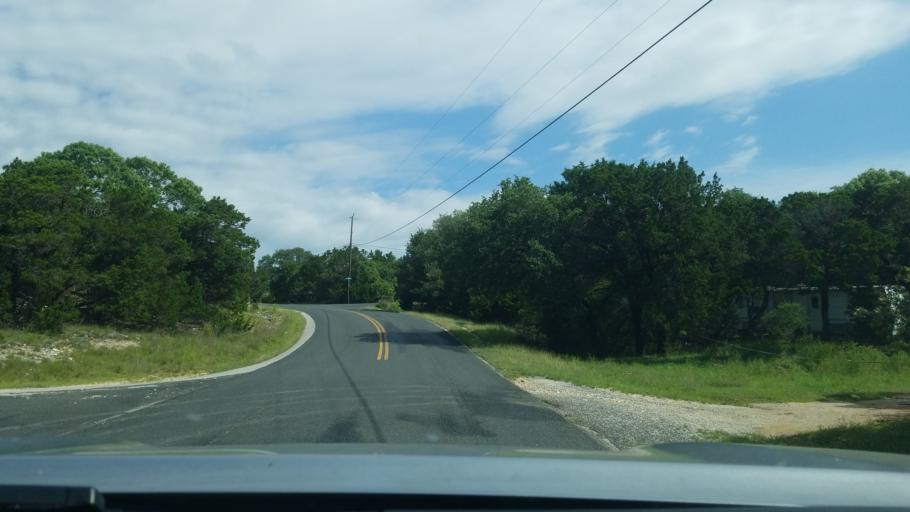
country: US
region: Texas
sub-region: Comal County
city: Bulverde
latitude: 29.7669
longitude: -98.4464
